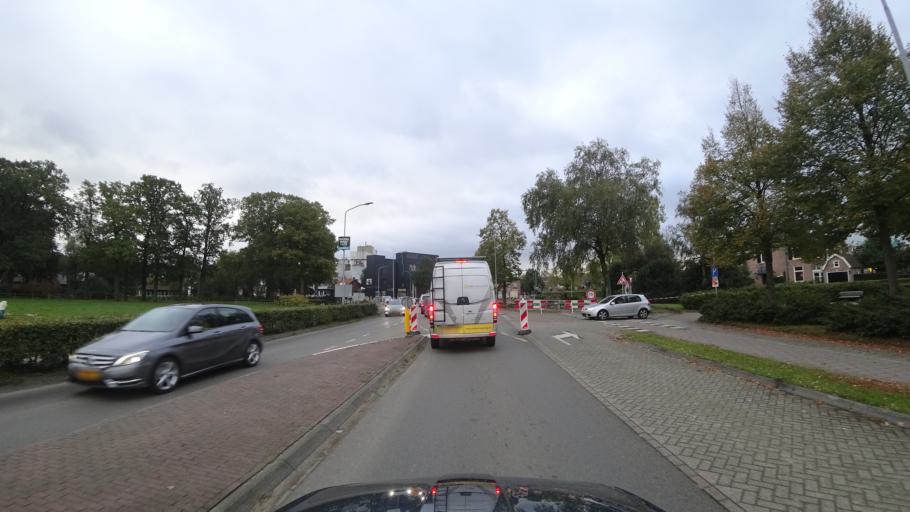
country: NL
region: Gelderland
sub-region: Gemeente Barneveld
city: Barneveld
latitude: 52.1425
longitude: 5.5894
